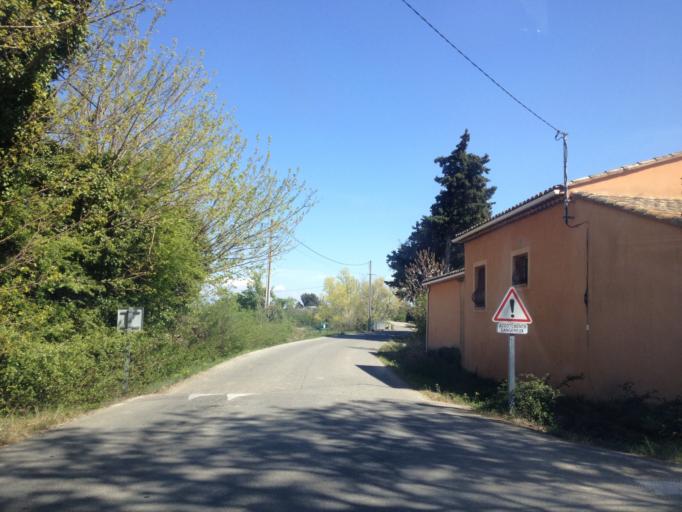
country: FR
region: Provence-Alpes-Cote d'Azur
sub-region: Departement du Vaucluse
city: Caderousse
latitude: 44.1112
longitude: 4.7849
